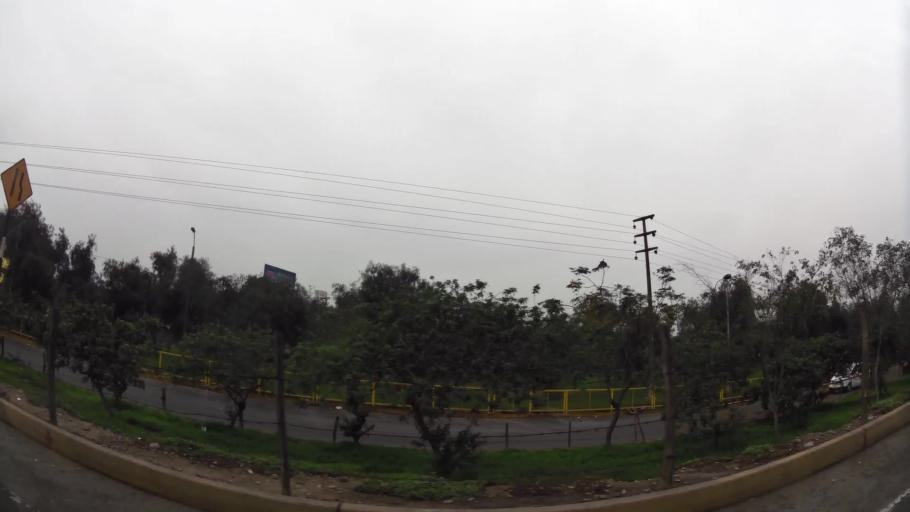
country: PE
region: Lima
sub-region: Lima
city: San Luis
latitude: -12.0841
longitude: -76.9840
